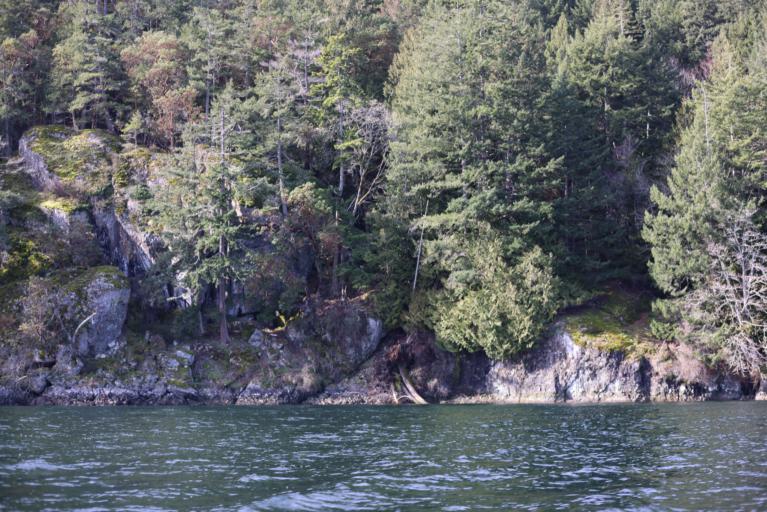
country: CA
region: British Columbia
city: North Cowichan
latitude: 48.7908
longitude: -123.5636
